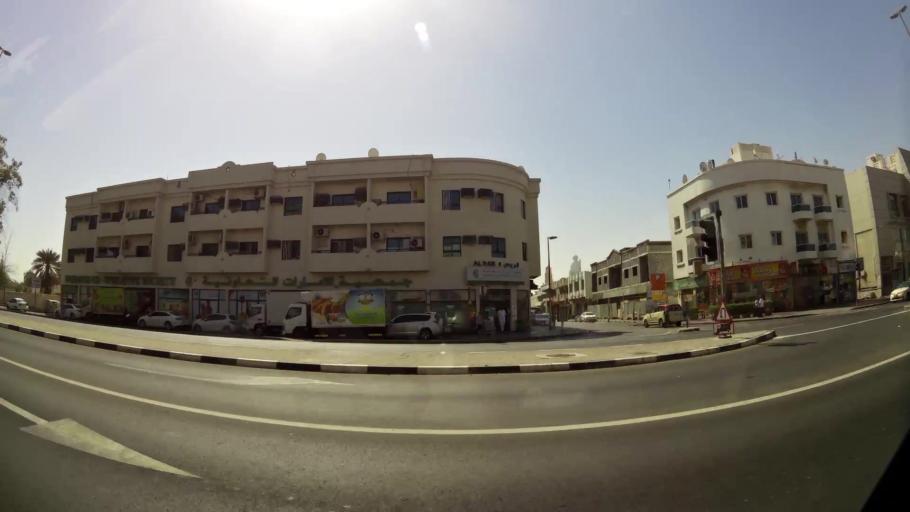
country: AE
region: Ash Shariqah
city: Sharjah
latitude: 25.2378
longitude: 55.2798
